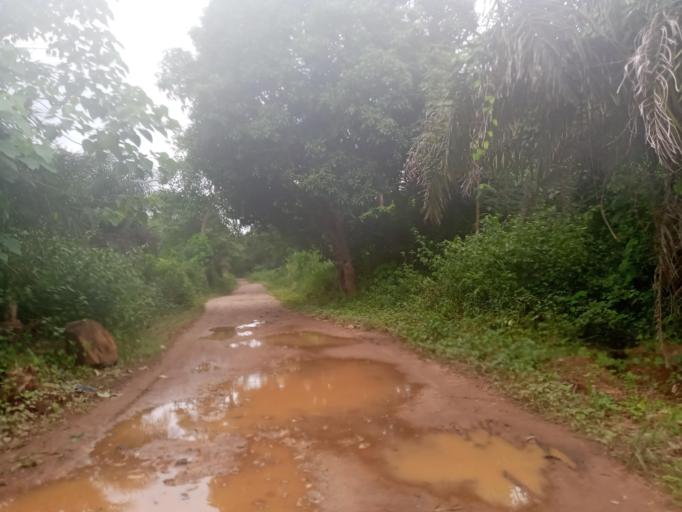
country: SL
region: Northern Province
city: Bumbuna
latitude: 8.9554
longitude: -11.7596
